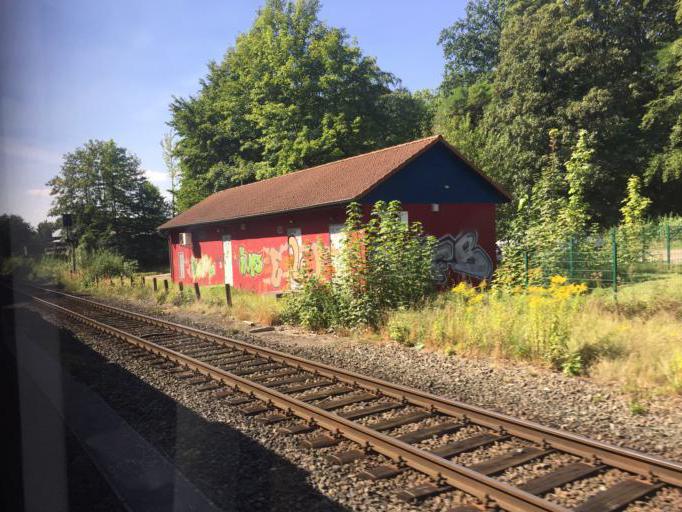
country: DE
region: Schleswig-Holstein
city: Bad Schwartau
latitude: 53.9148
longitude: 10.7011
